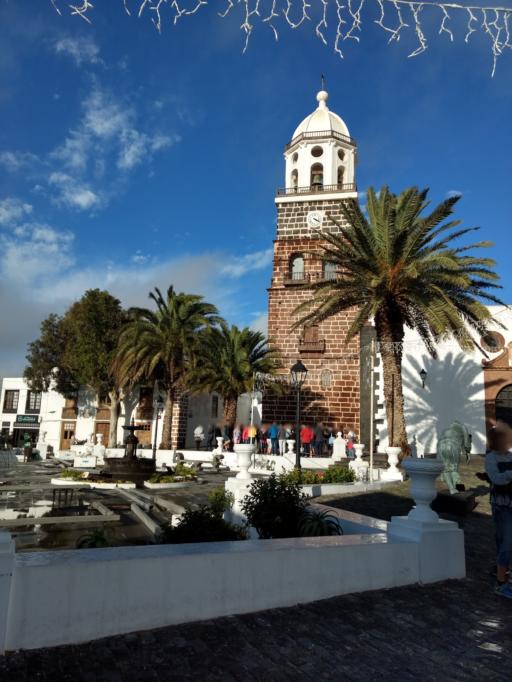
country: ES
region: Canary Islands
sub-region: Provincia de Las Palmas
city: Teguise
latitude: 29.0591
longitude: -13.5602
